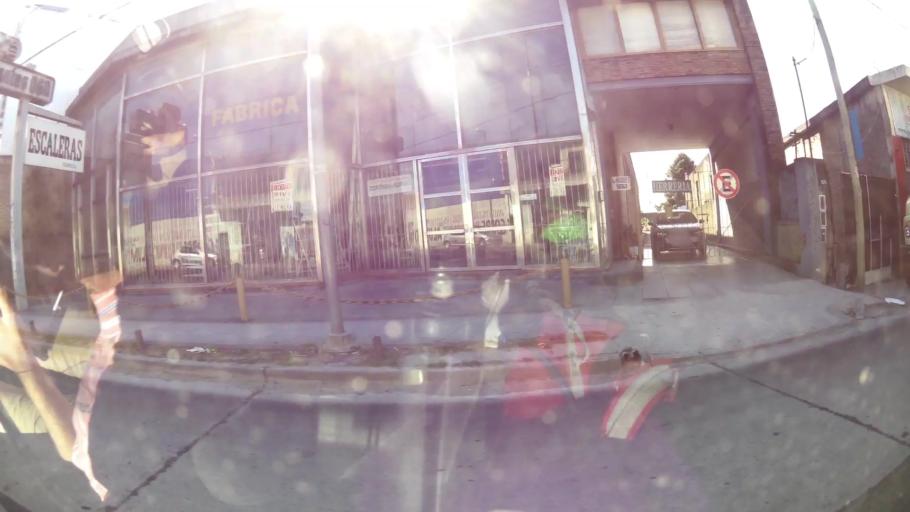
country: AR
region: Buenos Aires
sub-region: Partido de General San Martin
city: General San Martin
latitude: -34.5224
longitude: -58.5709
